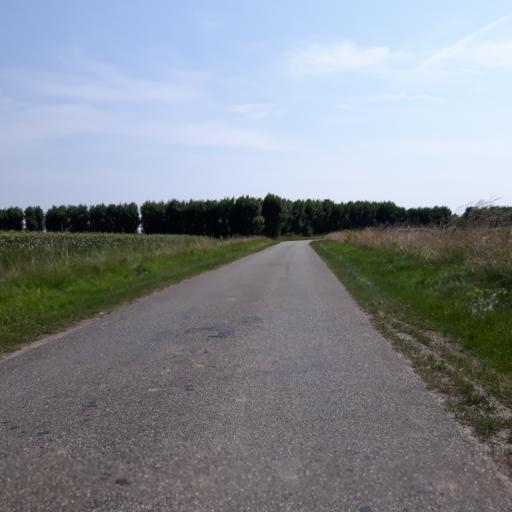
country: NL
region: Zeeland
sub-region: Gemeente Goes
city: Goes
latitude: 51.4691
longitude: 3.9083
